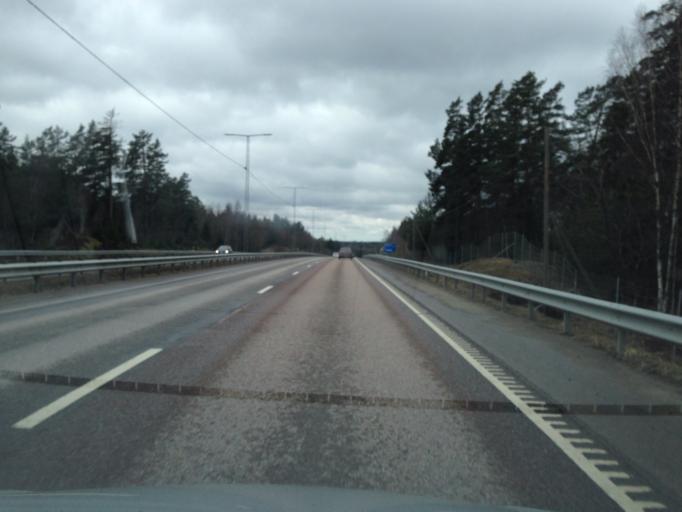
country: SE
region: Stockholm
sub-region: Vallentuna Kommun
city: Vallentuna
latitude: 59.4943
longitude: 18.1783
